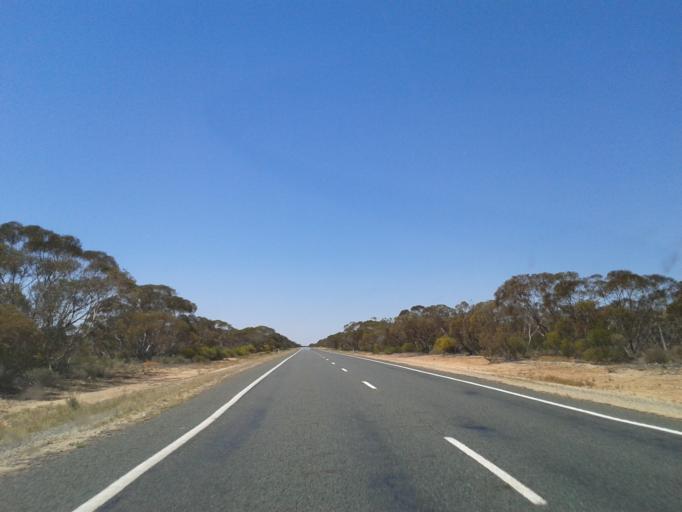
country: AU
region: New South Wales
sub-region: Wentworth
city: Gol Gol
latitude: -34.4488
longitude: 142.4896
